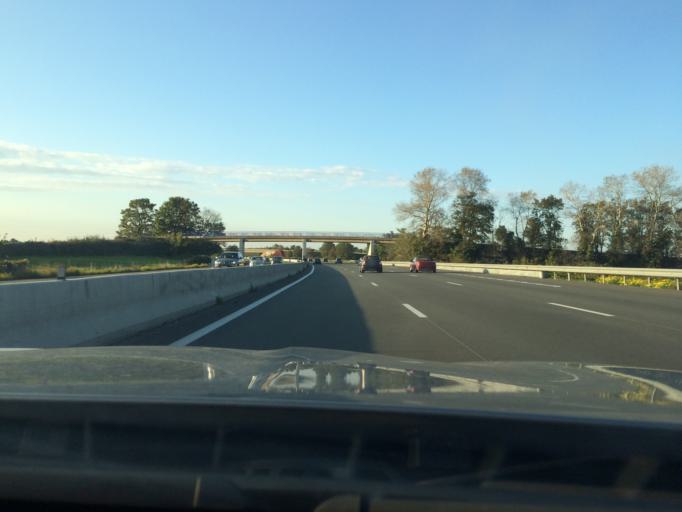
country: FR
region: Ile-de-France
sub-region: Departement de l'Essonne
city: Le Coudray-Montceaux
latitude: 48.5535
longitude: 2.4934
